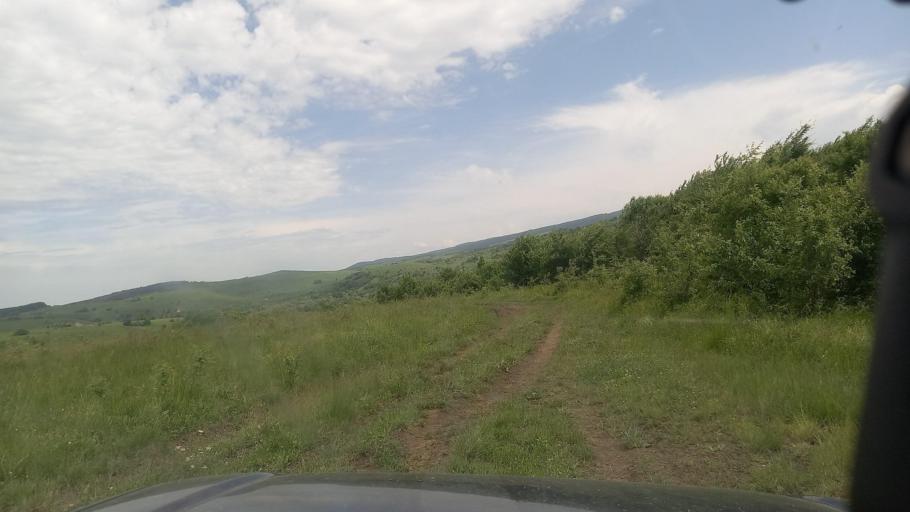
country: RU
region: Karachayevo-Cherkesiya
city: Pregradnaya
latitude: 44.0817
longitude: 41.2487
